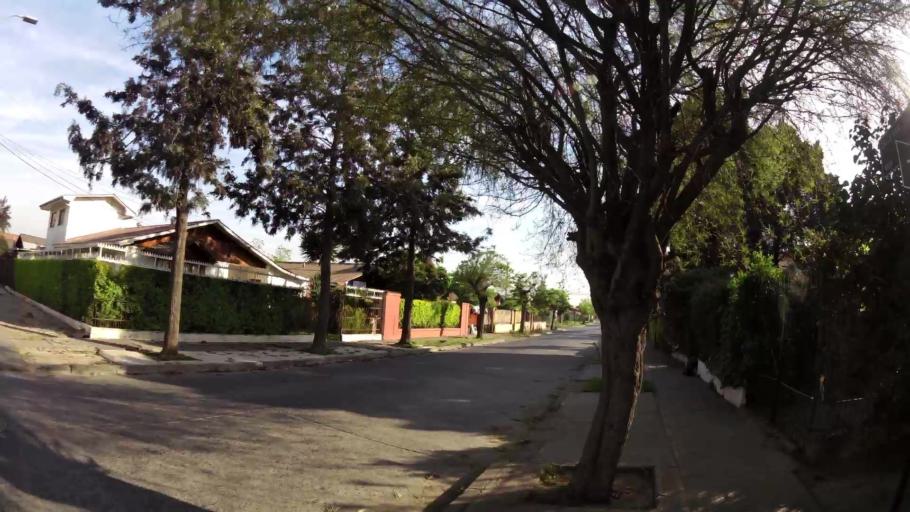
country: CL
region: Santiago Metropolitan
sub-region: Provincia de Santiago
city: Santiago
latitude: -33.5150
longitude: -70.6711
